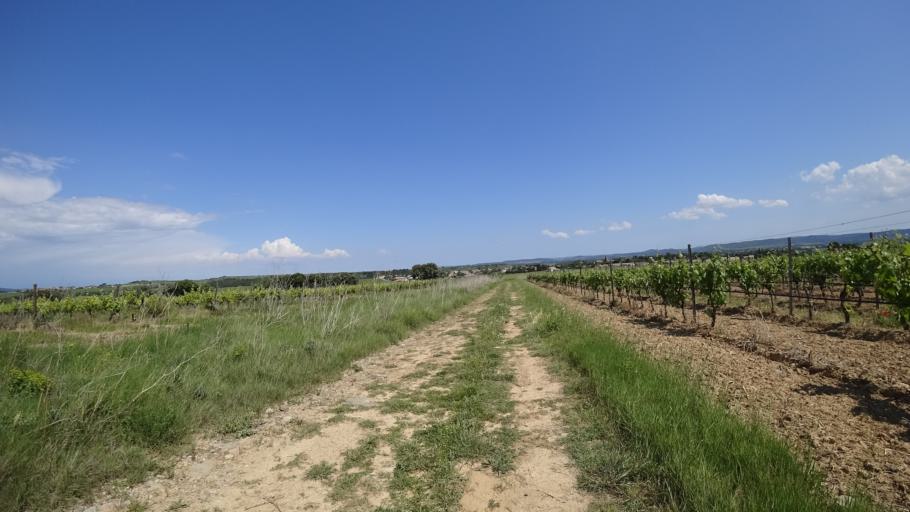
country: FR
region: Languedoc-Roussillon
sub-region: Departement de l'Aude
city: Canet
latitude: 43.2562
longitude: 2.8195
